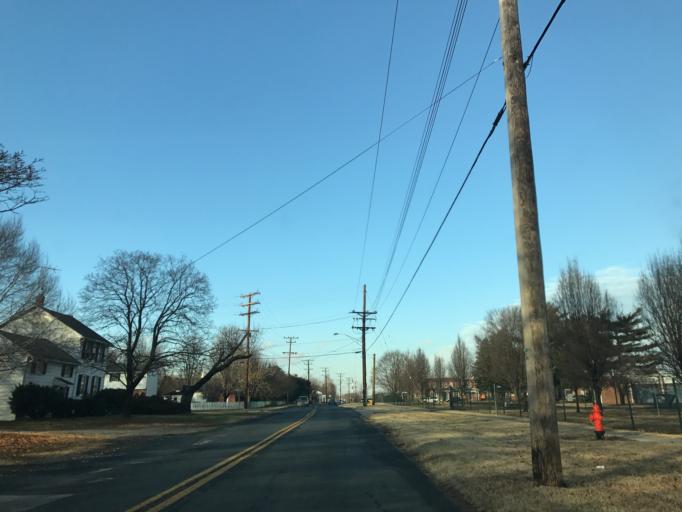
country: US
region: Maryland
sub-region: Baltimore County
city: Dundalk
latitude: 39.2686
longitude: -76.4948
